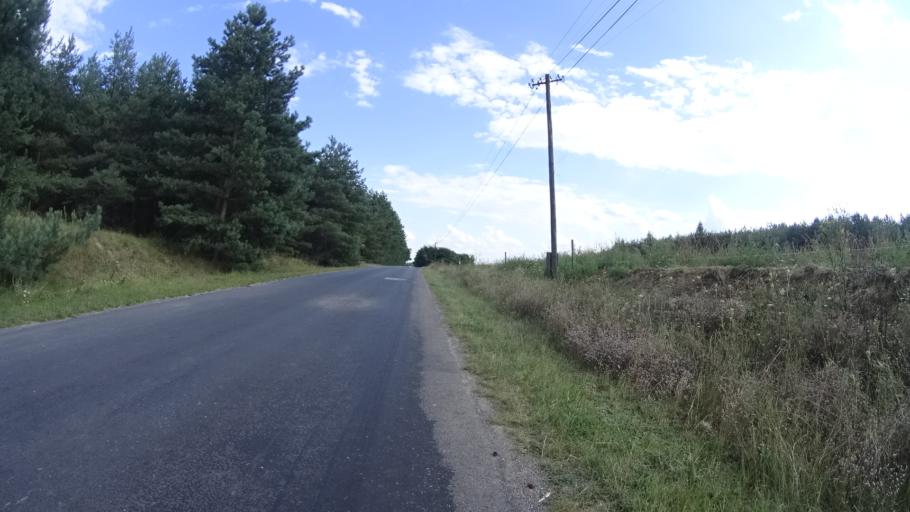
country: PL
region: Masovian Voivodeship
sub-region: Powiat grojecki
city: Mogielnica
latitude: 51.6865
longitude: 20.7542
